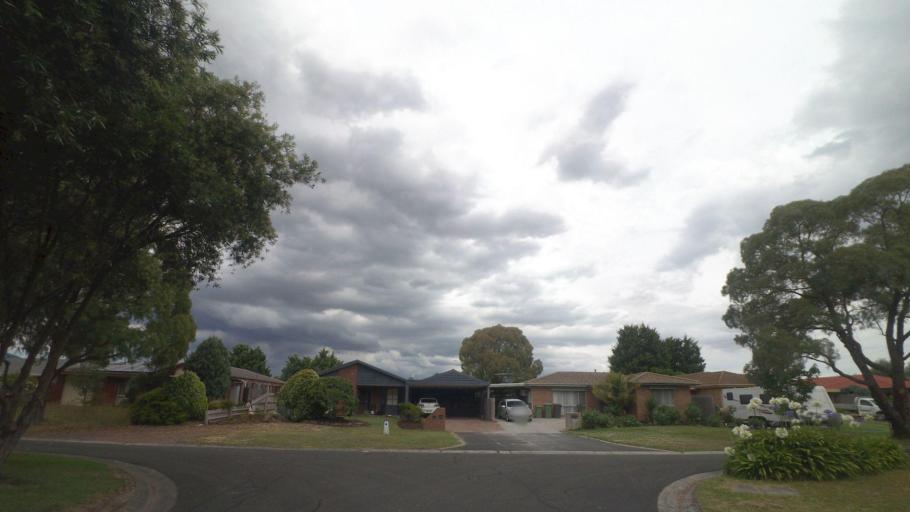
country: AU
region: Victoria
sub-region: Maroondah
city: Croydon South
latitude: -37.8203
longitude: 145.2821
